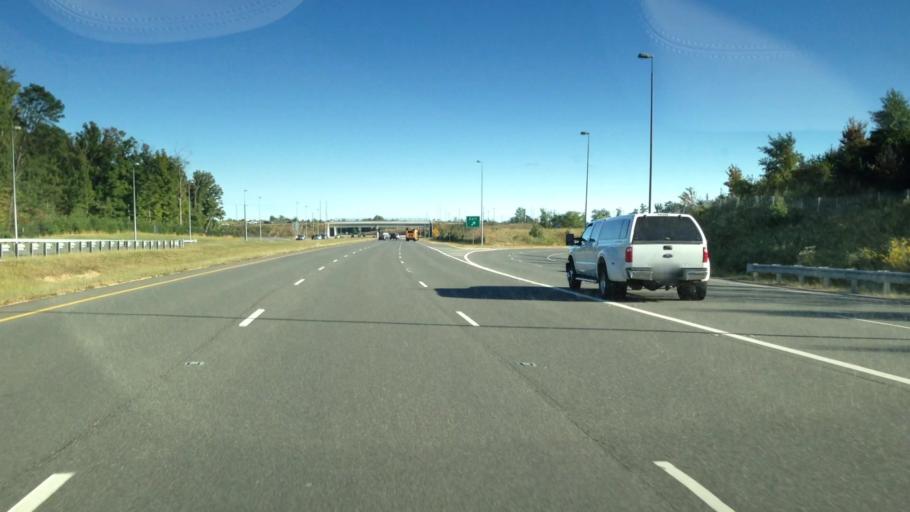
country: US
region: Virginia
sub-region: Fairfax County
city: West Springfield
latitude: 38.7509
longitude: -77.2130
